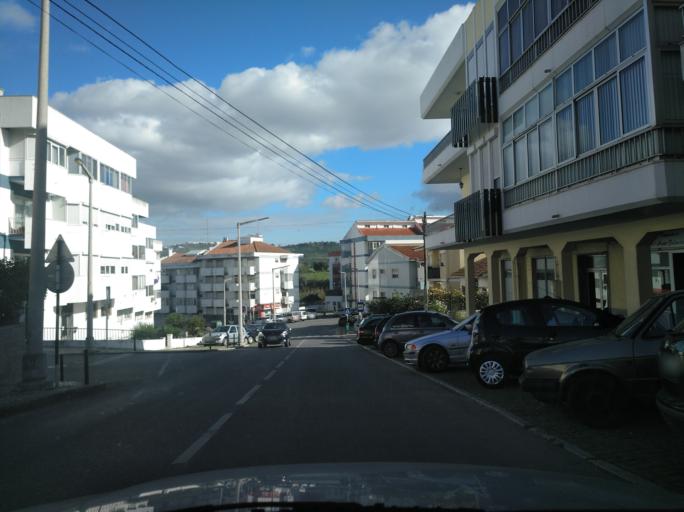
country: PT
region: Lisbon
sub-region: Loures
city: Loures
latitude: 38.8241
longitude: -9.1642
